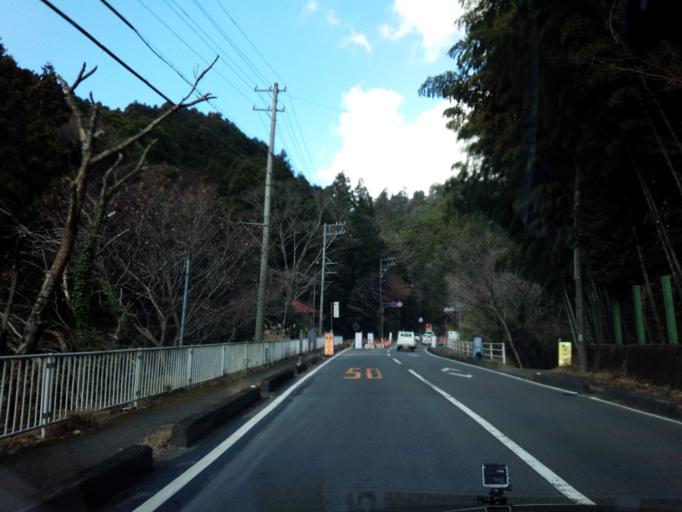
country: JP
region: Shizuoka
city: Fujinomiya
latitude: 35.1377
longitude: 138.5203
